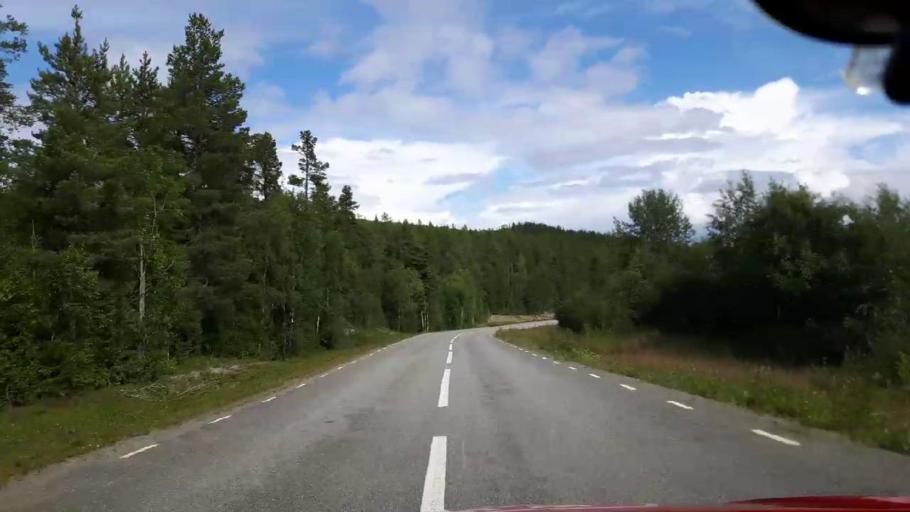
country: SE
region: Jaemtland
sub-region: Stroemsunds Kommun
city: Stroemsund
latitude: 64.3424
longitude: 15.1184
